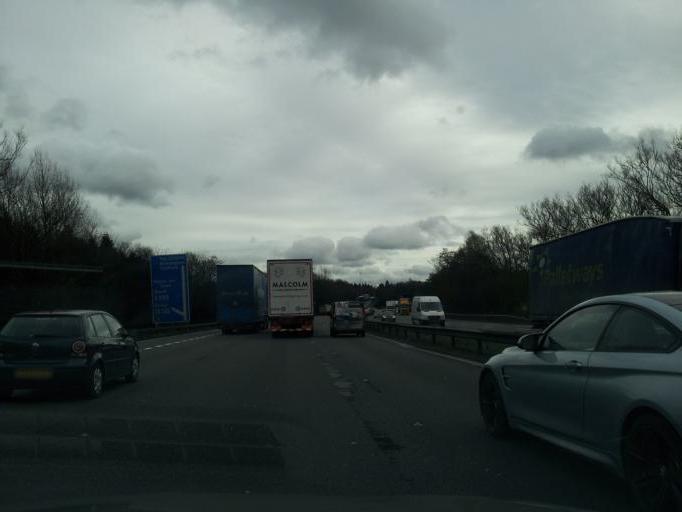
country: GB
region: England
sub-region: Staffordshire
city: Newcastle under Lyme
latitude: 52.9794
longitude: -2.2298
